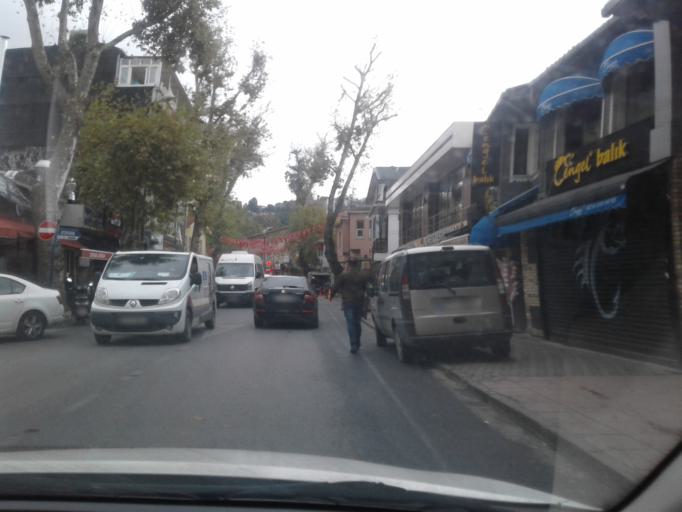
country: TR
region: Istanbul
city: UEskuedar
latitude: 41.0507
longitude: 29.0528
